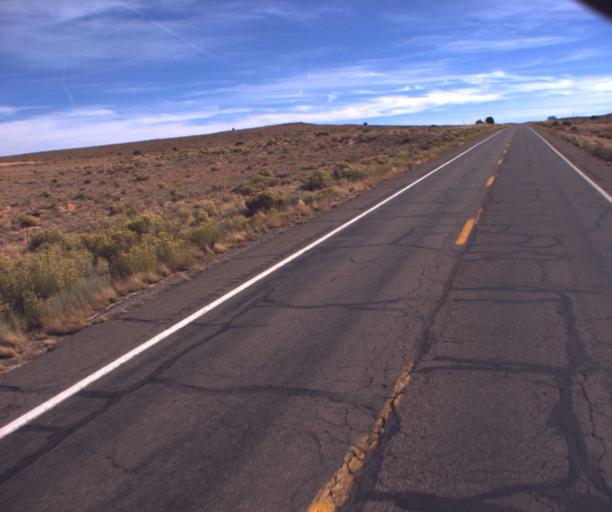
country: US
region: Arizona
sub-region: Coconino County
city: Kaibito
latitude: 36.6131
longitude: -111.0595
